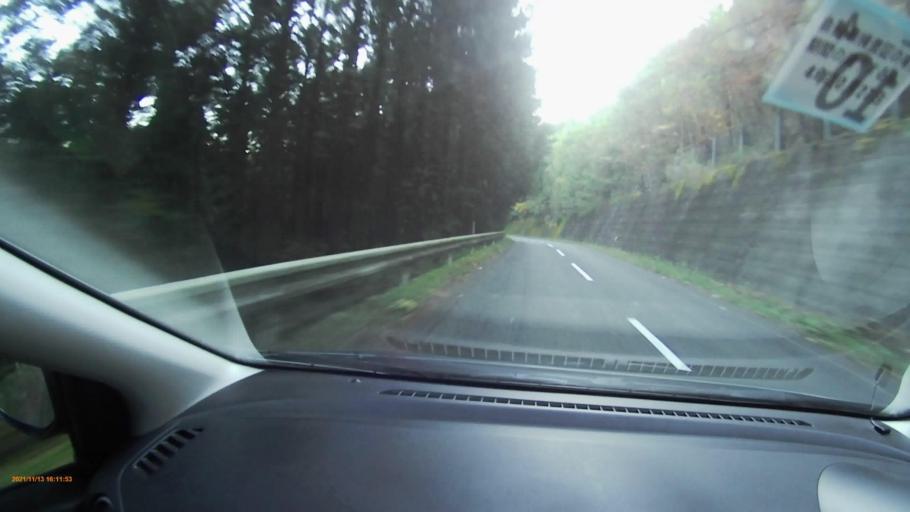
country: JP
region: Gifu
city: Nakatsugawa
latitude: 35.5854
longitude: 137.5092
